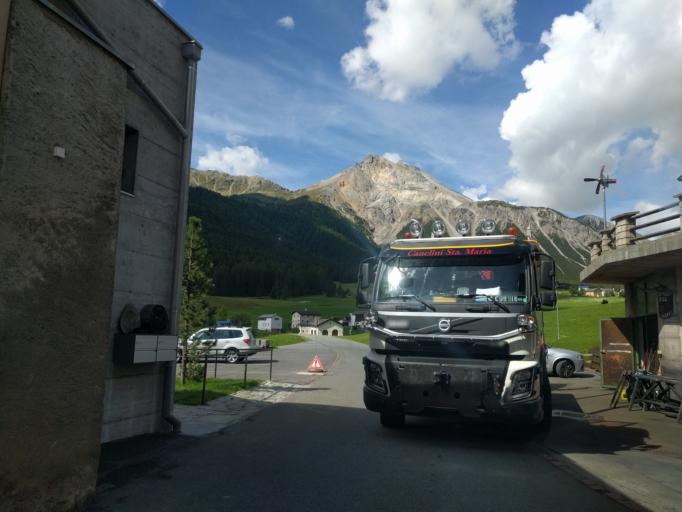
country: IT
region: Trentino-Alto Adige
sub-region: Bolzano
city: Tubre
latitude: 46.6284
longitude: 10.3362
